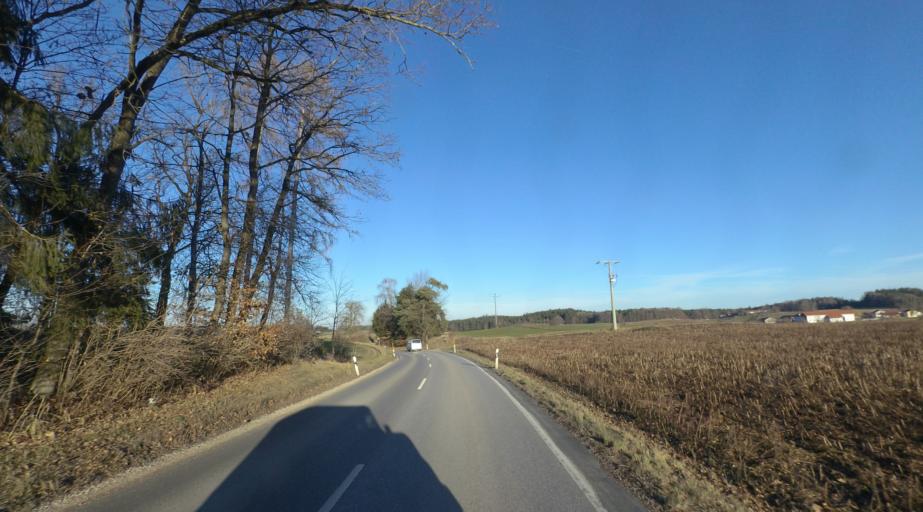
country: DE
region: Bavaria
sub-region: Upper Bavaria
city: Palling
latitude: 48.0059
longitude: 12.6853
